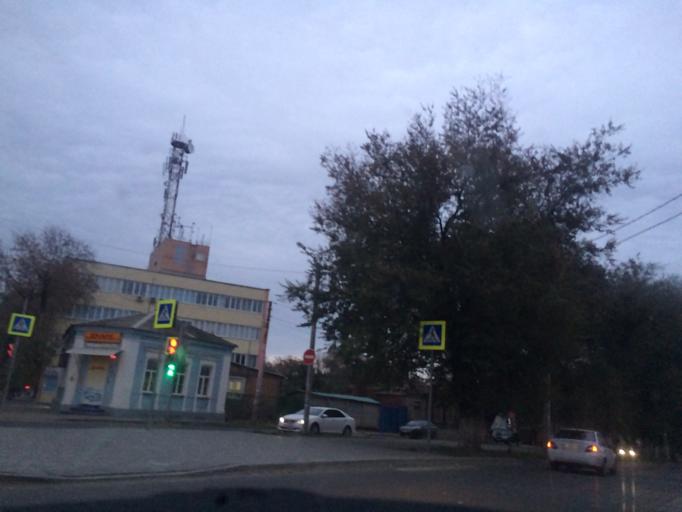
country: RU
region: Rostov
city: Novocherkassk
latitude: 47.4218
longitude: 40.0870
